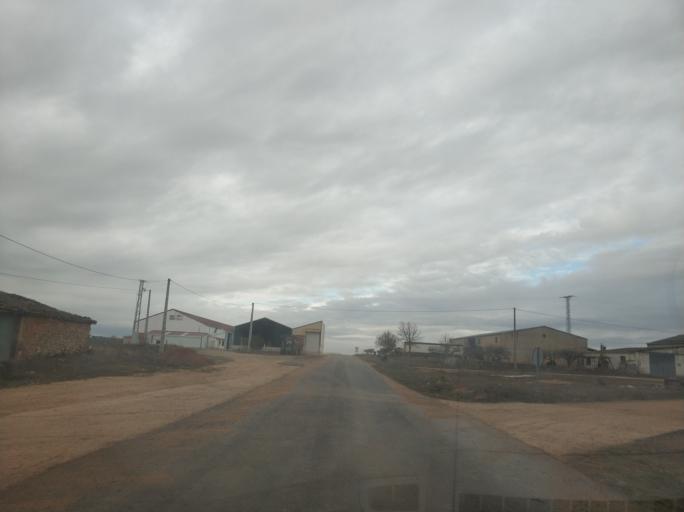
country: ES
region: Castille and Leon
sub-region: Provincia de Soria
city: Alcubilla de Avellaneda
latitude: 41.7241
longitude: -3.3087
